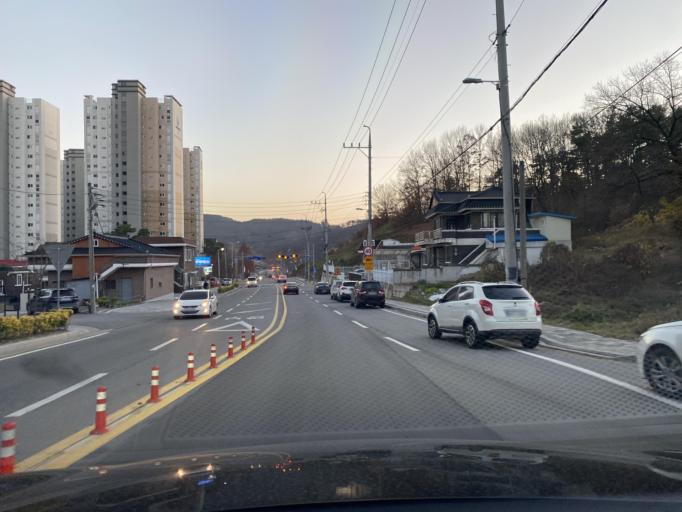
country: KR
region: Chungcheongnam-do
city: Yesan
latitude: 36.6840
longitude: 126.8437
